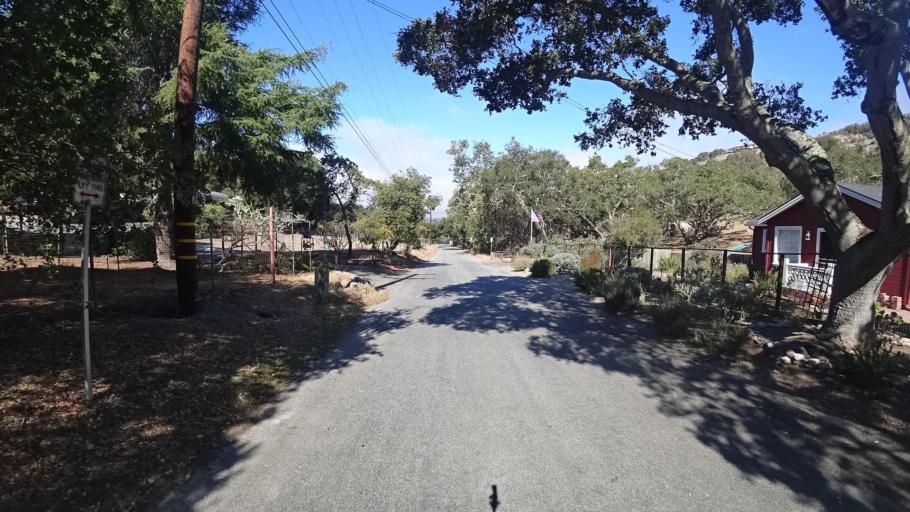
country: US
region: California
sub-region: Monterey County
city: Carmel Valley Village
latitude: 36.5652
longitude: -121.6968
